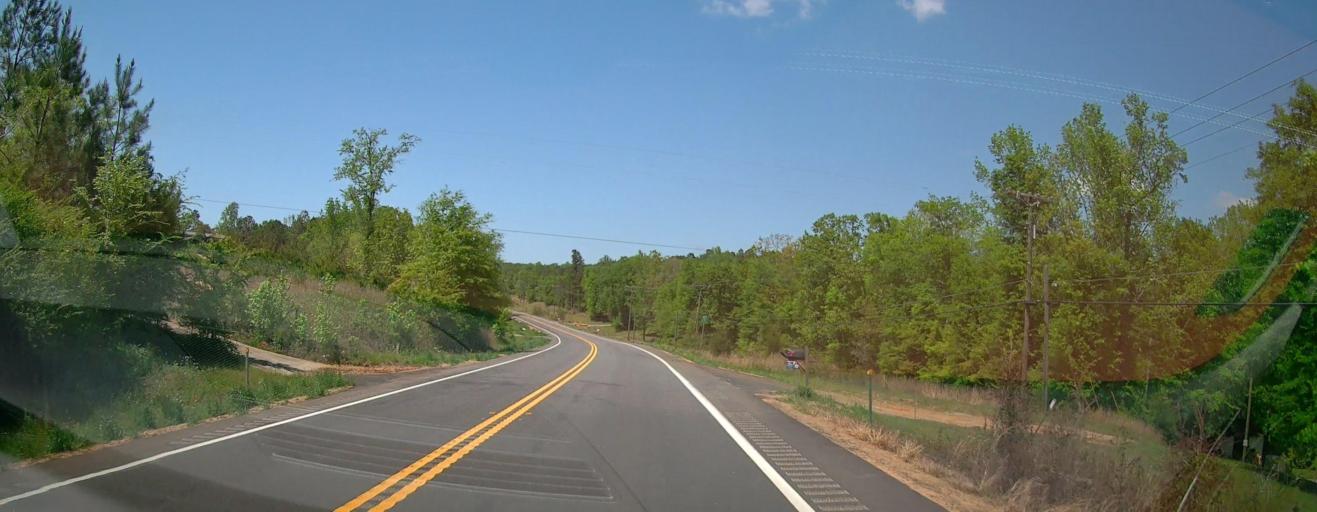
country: US
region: Georgia
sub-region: Putnam County
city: Eatonton
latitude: 33.2262
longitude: -83.4311
